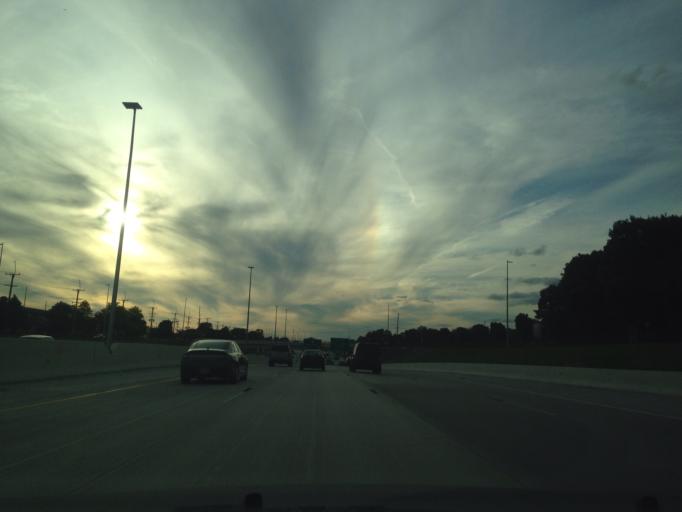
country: US
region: Michigan
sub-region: Wayne County
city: Livonia
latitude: 42.3819
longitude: -83.4071
